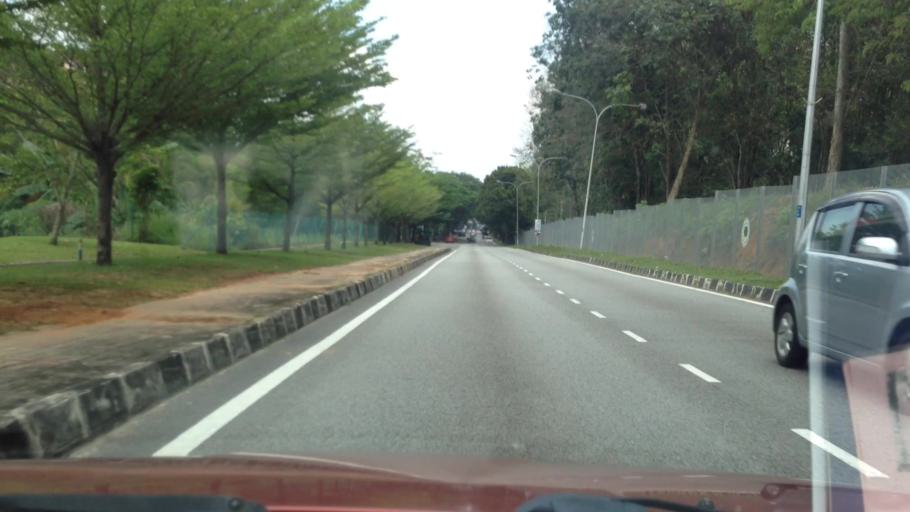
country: MY
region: Selangor
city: Kampung Baru Subang
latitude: 3.1680
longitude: 101.5512
